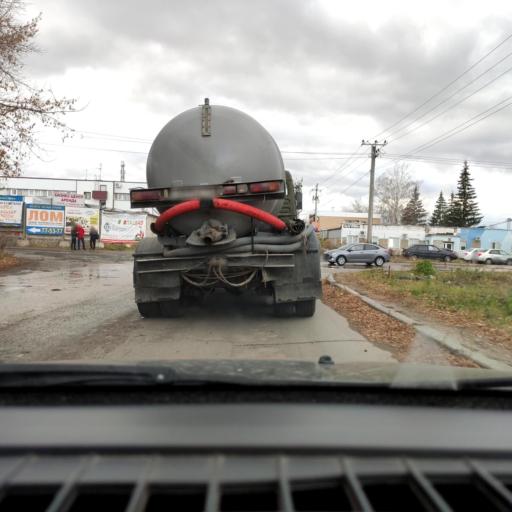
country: RU
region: Samara
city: Tol'yatti
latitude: 53.5702
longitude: 49.2878
